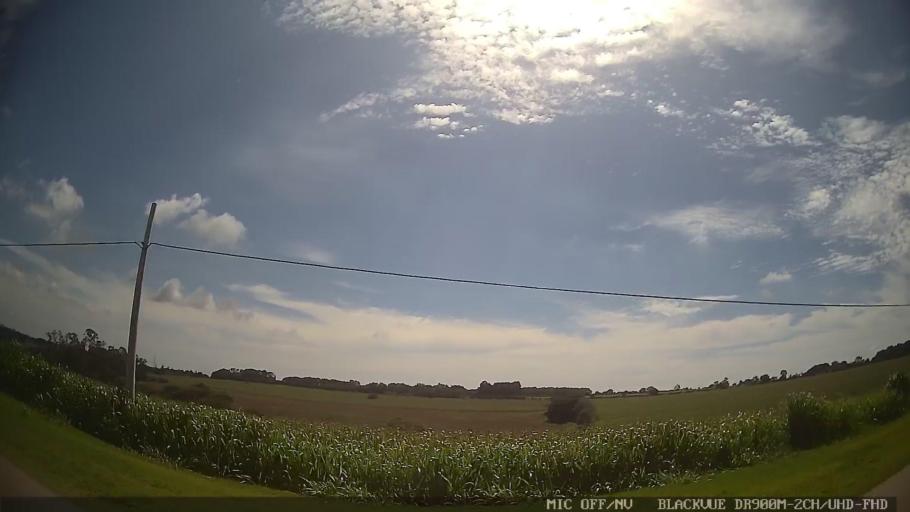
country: BR
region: Sao Paulo
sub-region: Tiete
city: Tiete
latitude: -23.1261
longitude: -47.6978
